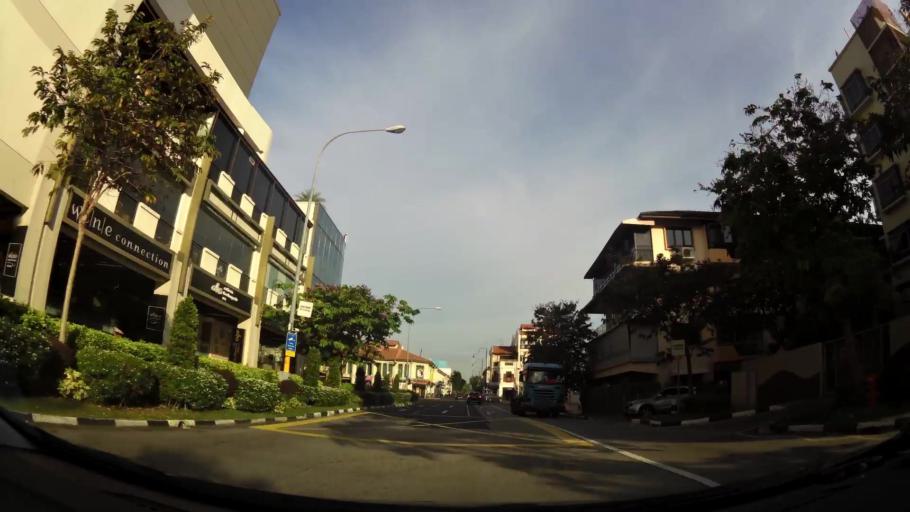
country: SG
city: Singapore
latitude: 1.3053
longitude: 103.9053
